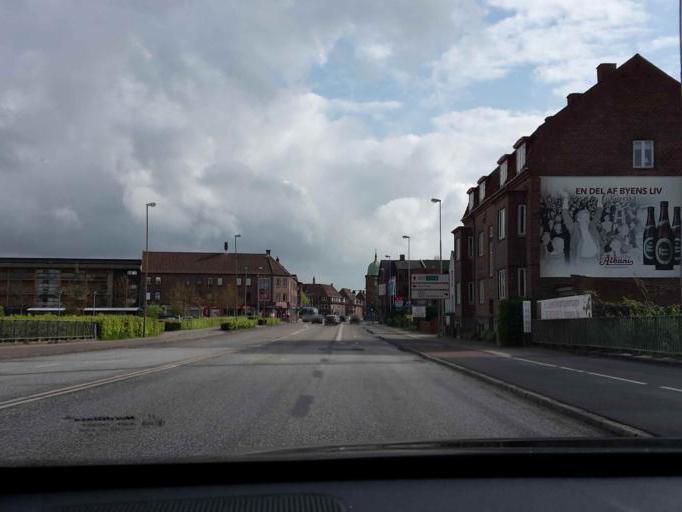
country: DK
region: South Denmark
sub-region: Odense Kommune
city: Odense
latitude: 55.4005
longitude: 10.3677
